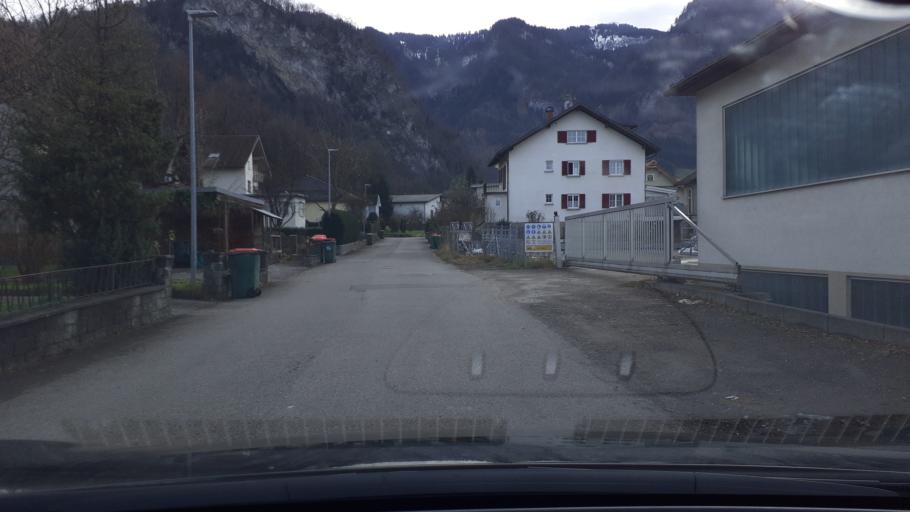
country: AT
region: Vorarlberg
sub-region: Politischer Bezirk Dornbirn
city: Hohenems
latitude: 47.3662
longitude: 9.6843
